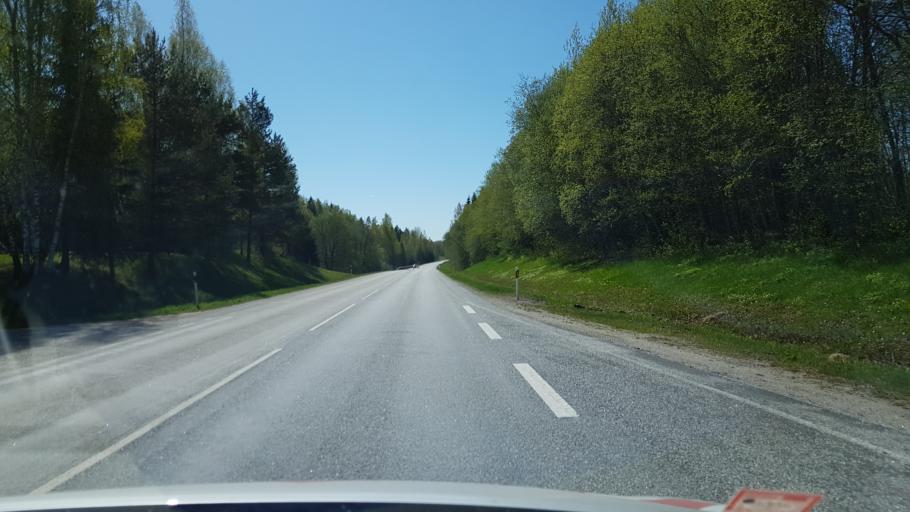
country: RU
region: Pskov
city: Pechory
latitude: 57.6513
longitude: 27.3354
